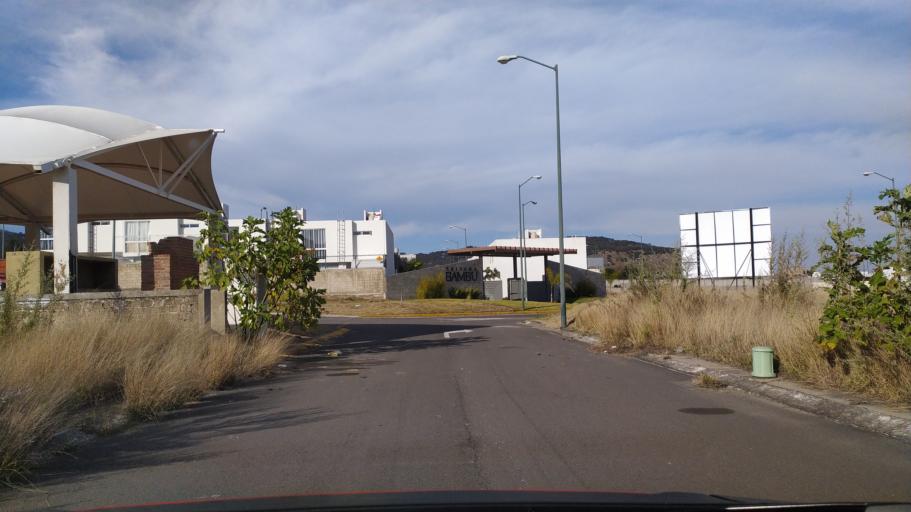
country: MX
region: Jalisco
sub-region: Tlajomulco de Zuniga
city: Palomar
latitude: 20.6324
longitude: -103.4830
